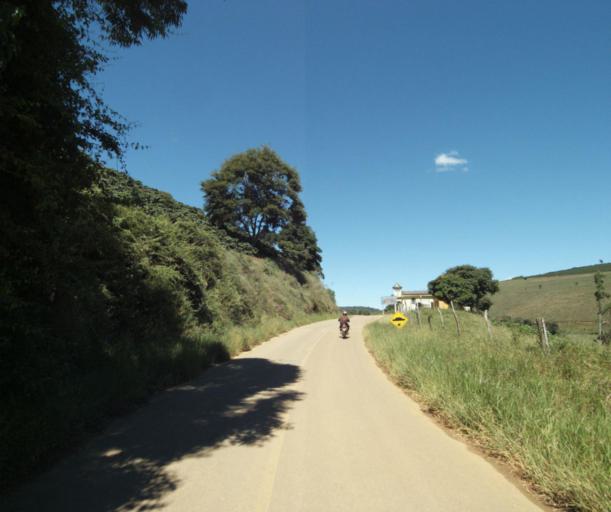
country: BR
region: Minas Gerais
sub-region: Espera Feliz
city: Espera Feliz
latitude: -20.5929
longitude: -41.8384
